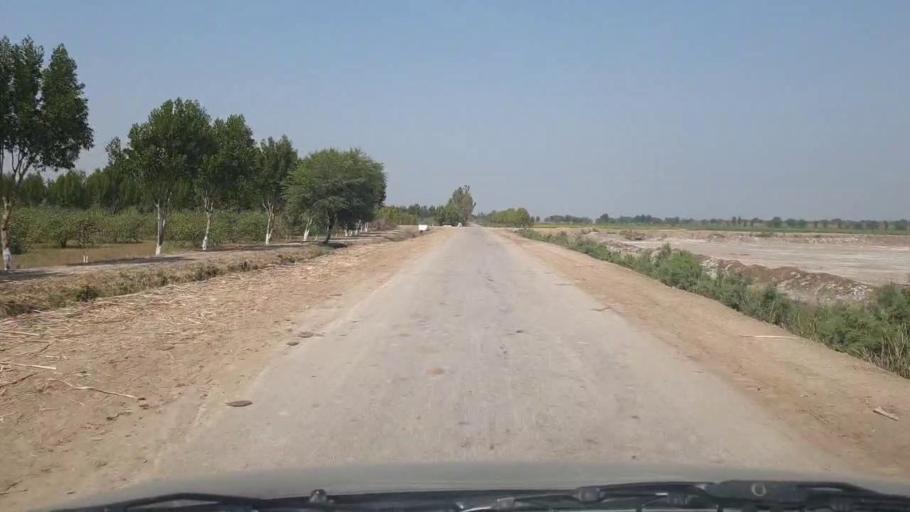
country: PK
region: Sindh
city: Mirwah Gorchani
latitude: 25.3637
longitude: 69.1438
